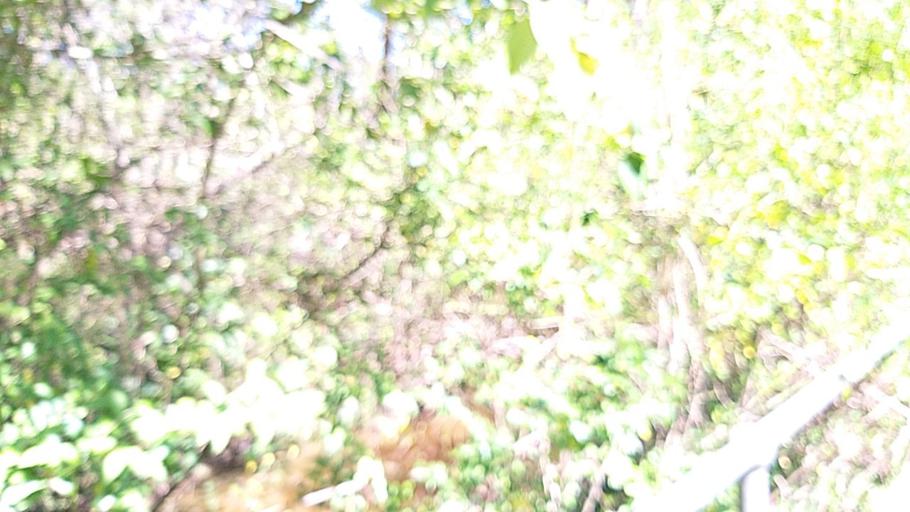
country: AU
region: New South Wales
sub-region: Ryde
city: East Ryde
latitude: -33.8162
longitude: 151.1315
